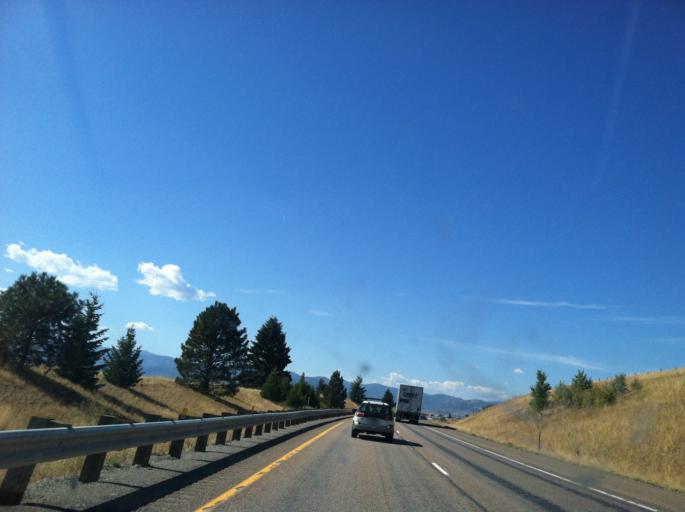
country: US
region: Montana
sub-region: Missoula County
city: Orchard Homes
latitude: 46.9389
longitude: -114.1050
